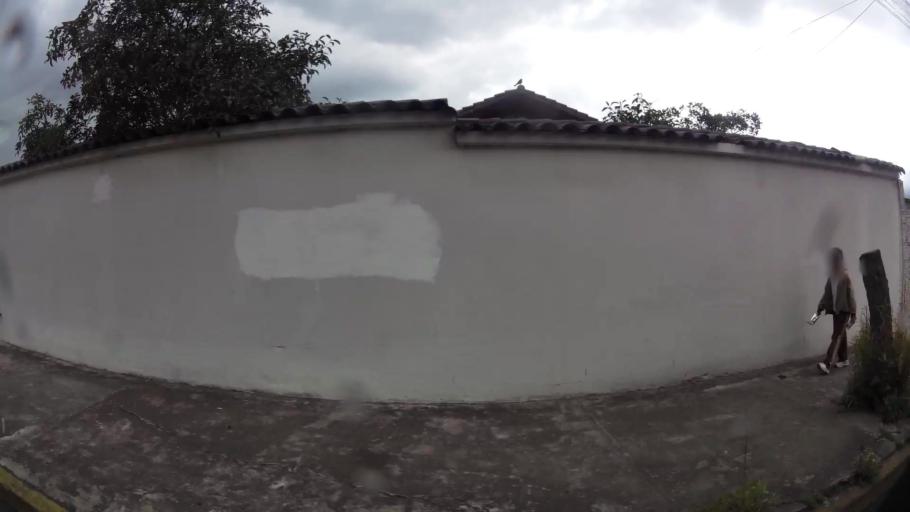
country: EC
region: Pichincha
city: Quito
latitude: -0.1050
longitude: -78.4821
